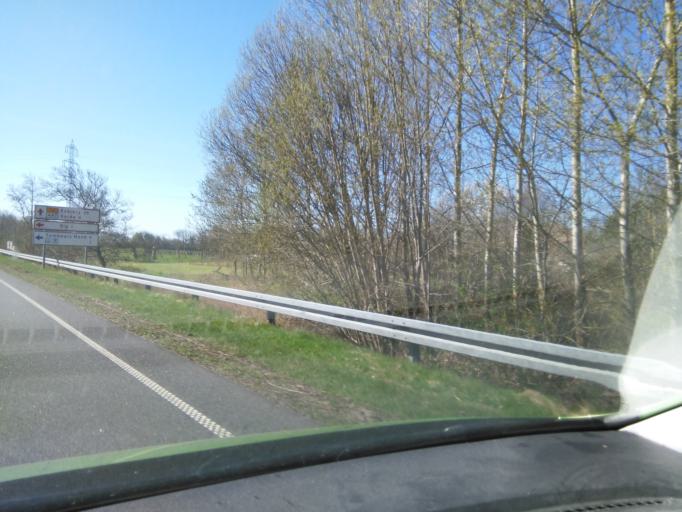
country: DK
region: South Denmark
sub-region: Varde Kommune
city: Varde
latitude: 55.6650
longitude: 8.5668
